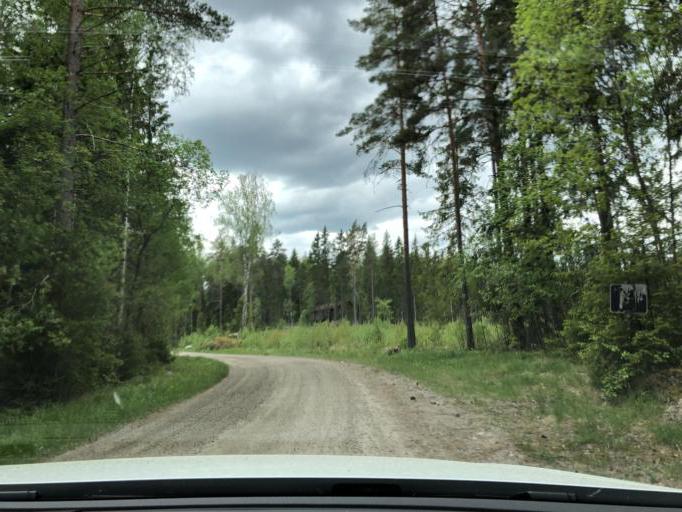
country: SE
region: Uppsala
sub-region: Heby Kommun
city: Heby
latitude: 60.0549
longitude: 16.7809
